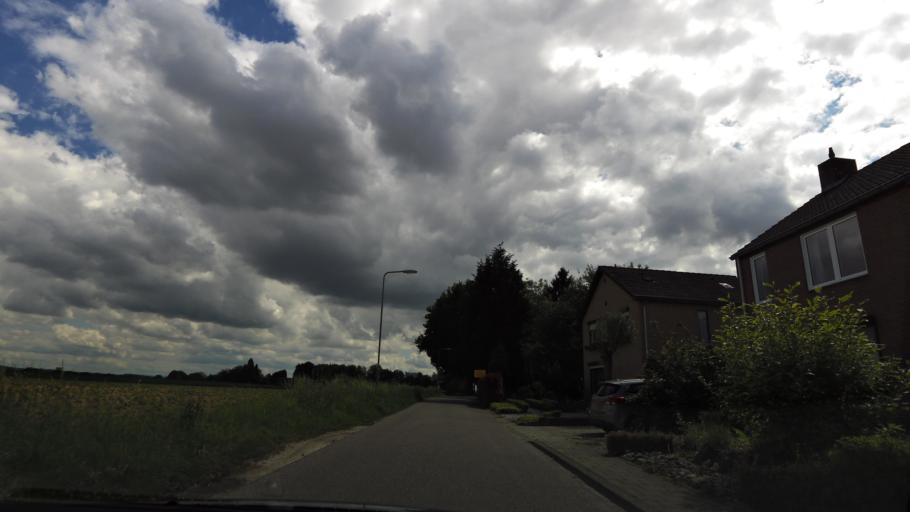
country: NL
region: Limburg
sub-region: Gemeente Schinnen
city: Oirsbeek
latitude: 50.9570
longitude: 5.9126
